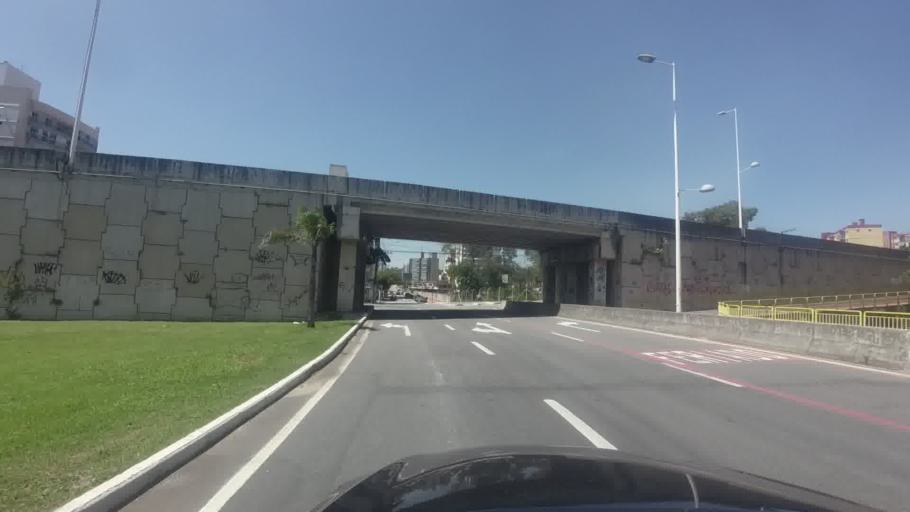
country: BR
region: Espirito Santo
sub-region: Vila Velha
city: Vila Velha
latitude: -20.2644
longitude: -40.2610
